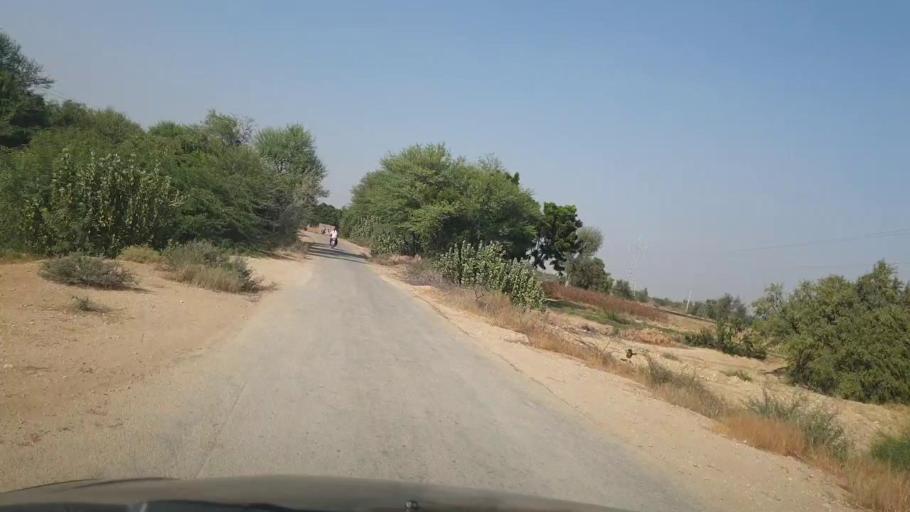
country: PK
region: Sindh
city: Jamshoro
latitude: 25.5253
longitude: 67.8220
